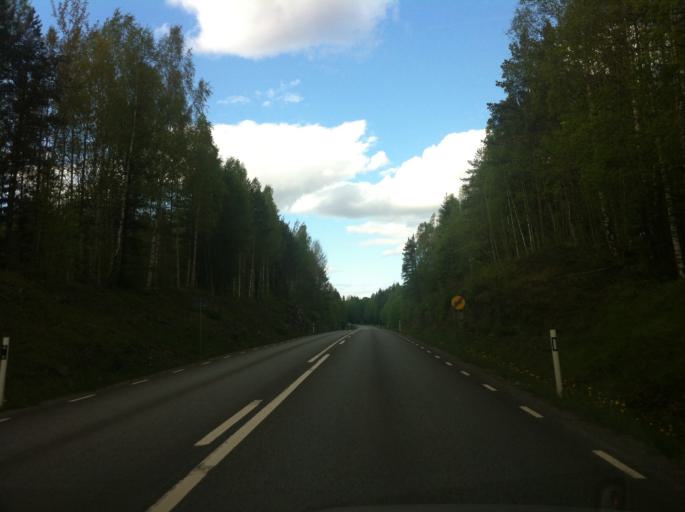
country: SE
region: Vaermland
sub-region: Filipstads Kommun
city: Filipstad
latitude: 59.7531
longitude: 14.2469
